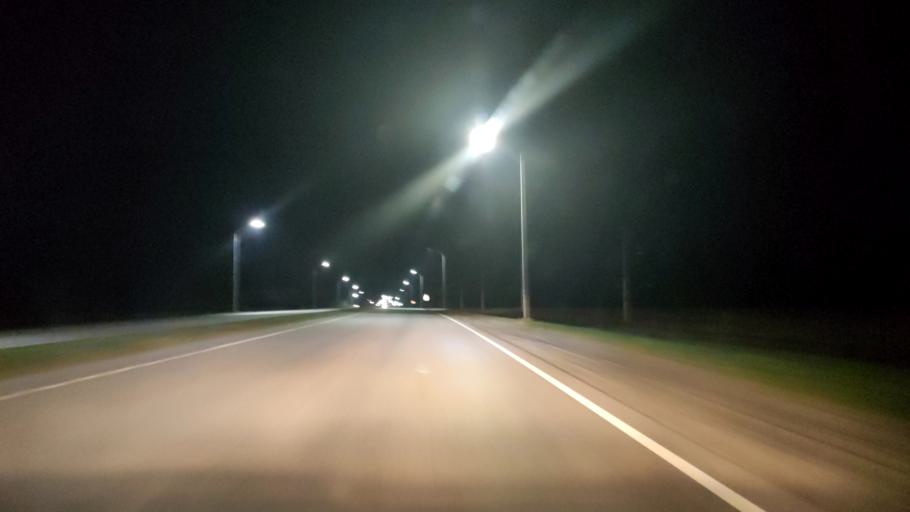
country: RU
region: Belgorod
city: Staryy Oskol
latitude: 51.3957
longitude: 37.8717
